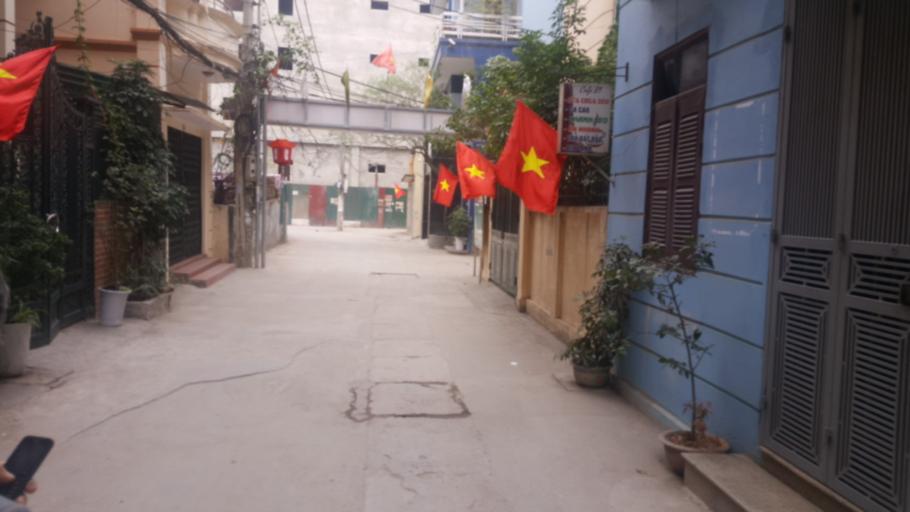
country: VN
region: Ha Noi
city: Cau Giay
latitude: 21.0287
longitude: 105.7961
